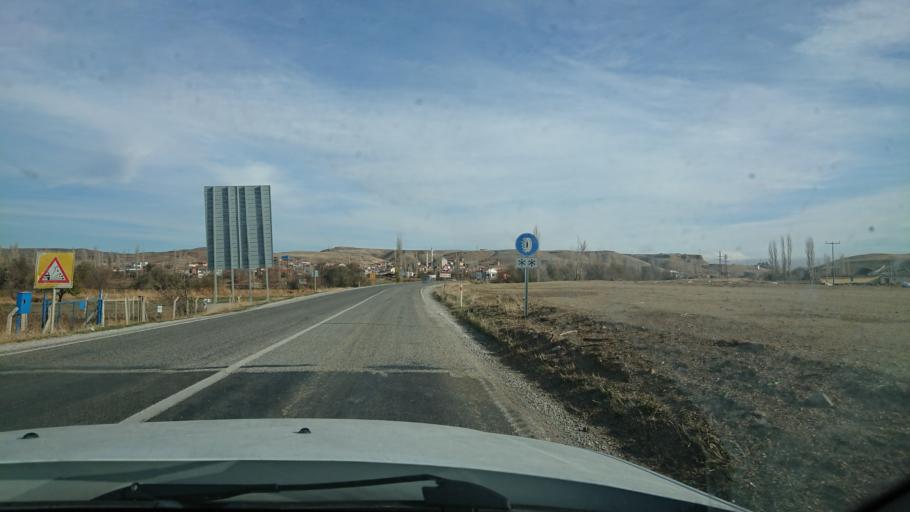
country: TR
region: Aksaray
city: Acipinar
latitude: 38.4803
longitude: 33.9020
